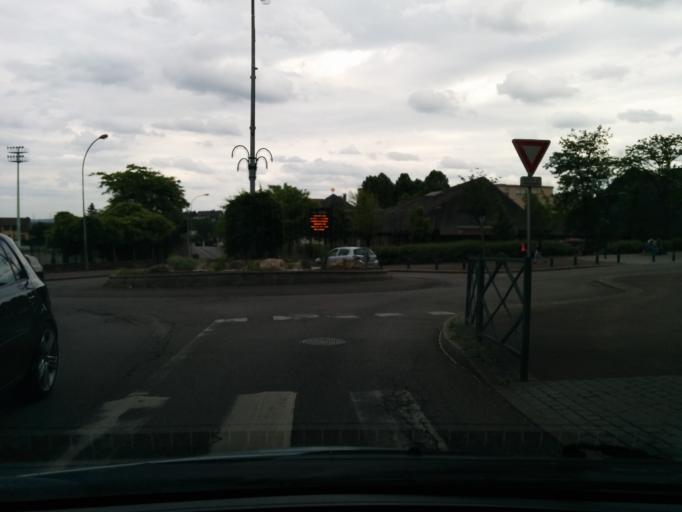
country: FR
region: Ile-de-France
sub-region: Departement des Yvelines
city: Mantes-la-Ville
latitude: 48.9774
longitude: 1.7032
